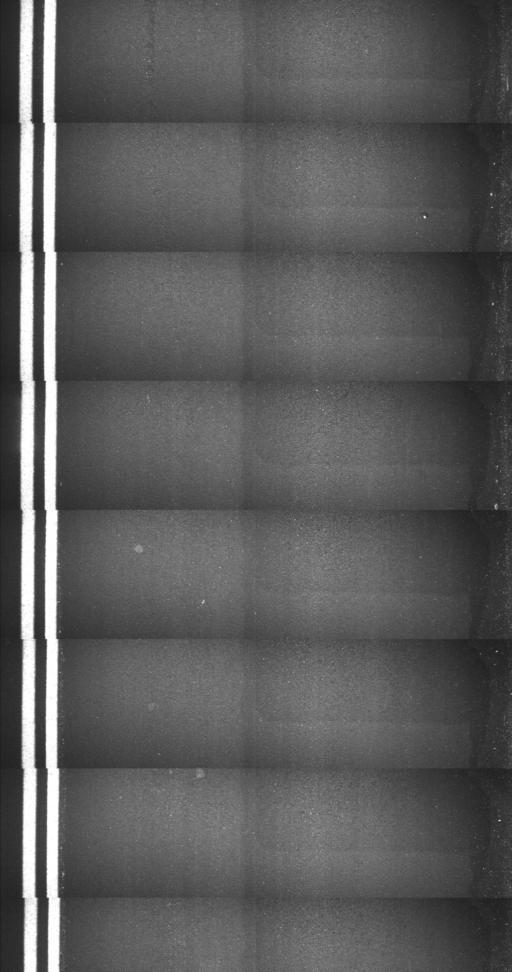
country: US
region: Vermont
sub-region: Windsor County
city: Woodstock
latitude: 43.5986
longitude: -72.5190
